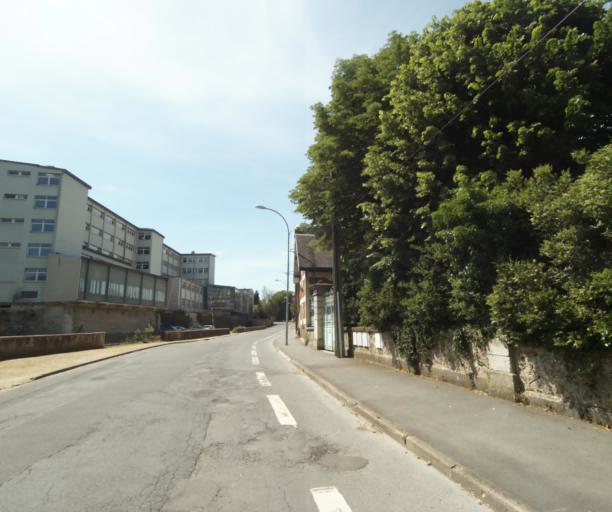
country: FR
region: Champagne-Ardenne
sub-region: Departement des Ardennes
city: Charleville-Mezieres
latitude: 49.7623
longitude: 4.7140
